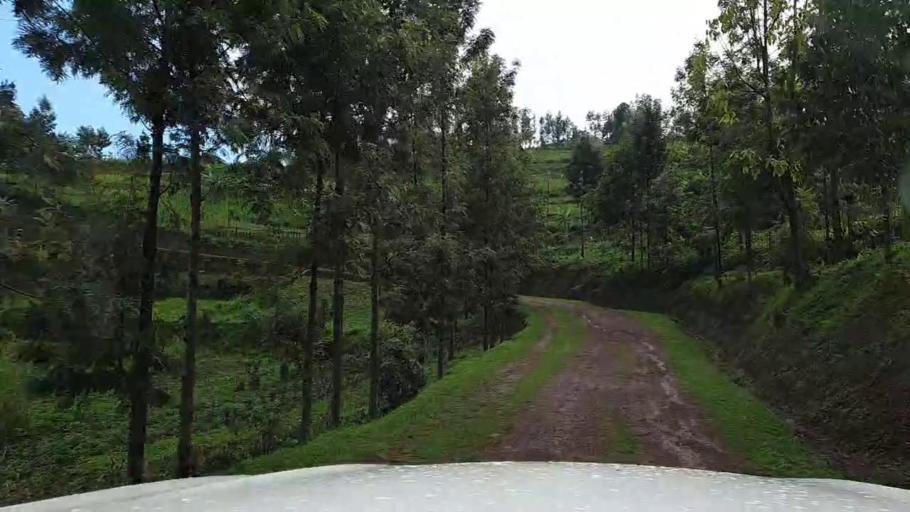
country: RW
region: Northern Province
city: Byumba
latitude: -1.7181
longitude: 29.9091
